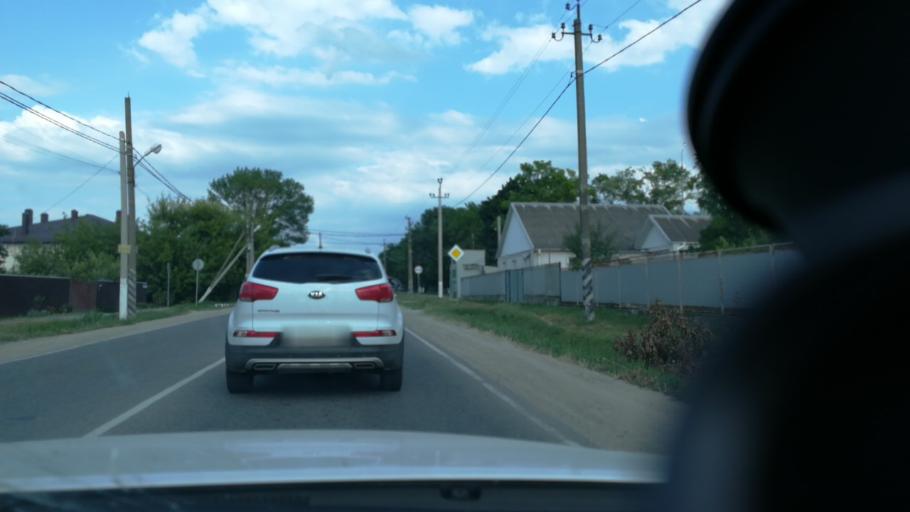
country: RU
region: Krasnodarskiy
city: Gostagayevskaya
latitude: 45.0258
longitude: 37.4996
